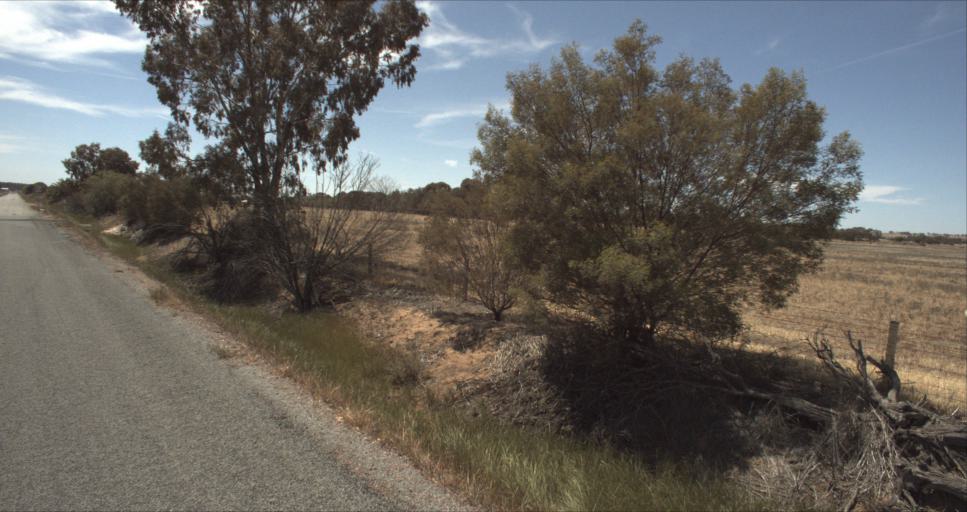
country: AU
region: New South Wales
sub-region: Leeton
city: Leeton
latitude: -34.6030
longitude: 146.4153
